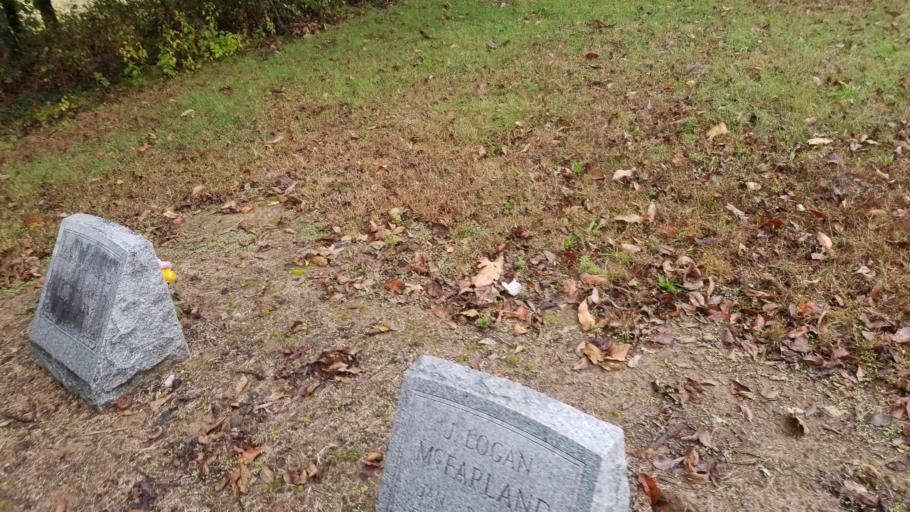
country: US
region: Illinois
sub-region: Saline County
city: Harrisburg
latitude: 37.8937
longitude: -88.6725
